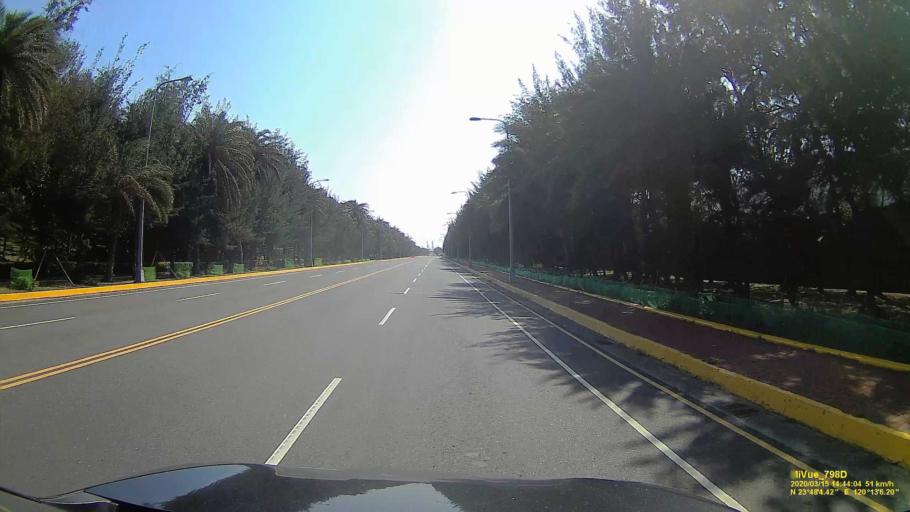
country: TW
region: Taiwan
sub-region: Yunlin
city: Douliu
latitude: 23.8011
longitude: 120.2182
